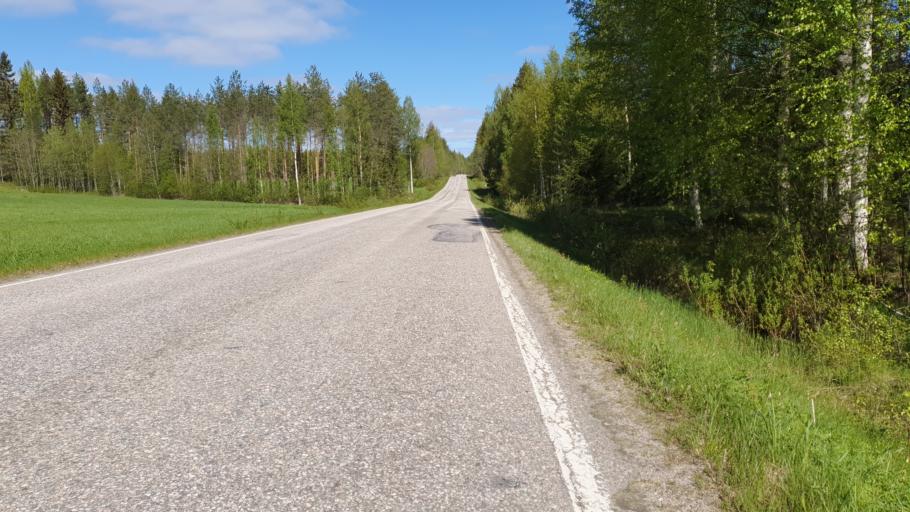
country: FI
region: Kainuu
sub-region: Kehys-Kainuu
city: Kuhmo
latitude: 64.1808
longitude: 29.4484
